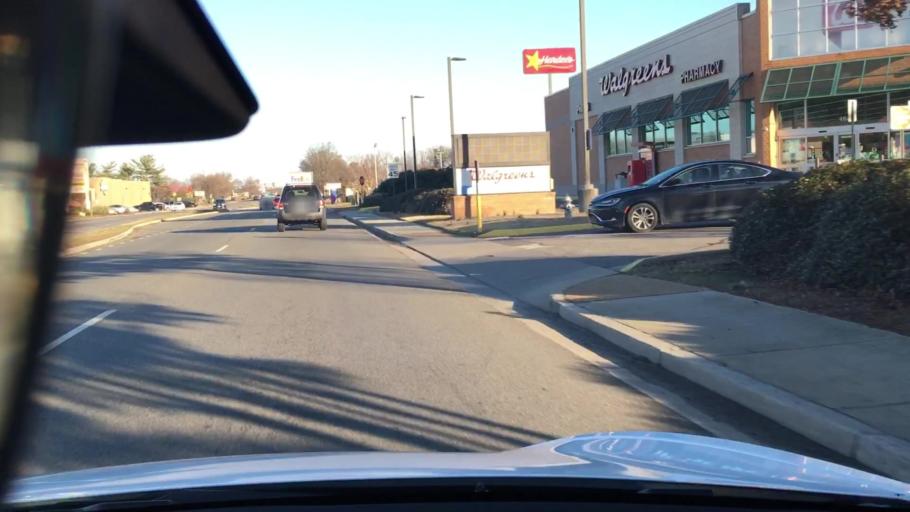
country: US
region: Virginia
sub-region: Henrico County
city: Fort Lee
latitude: 37.5180
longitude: -77.3502
